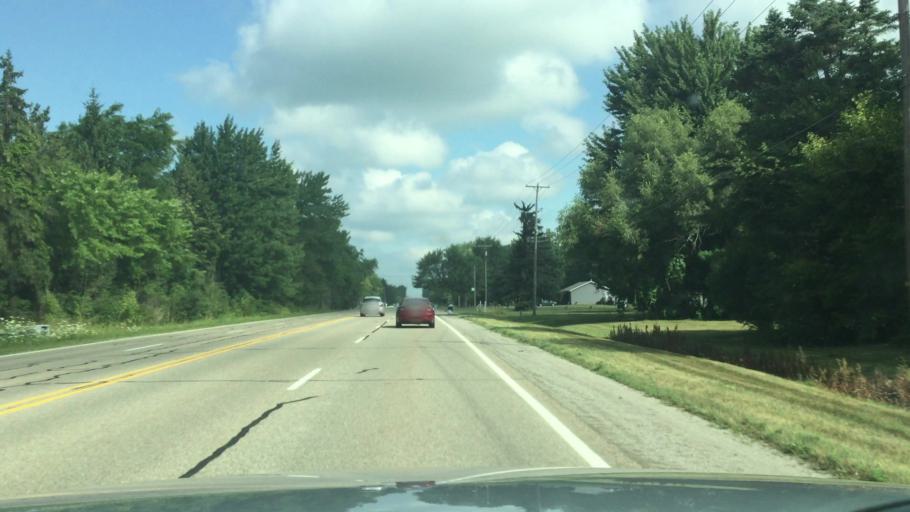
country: US
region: Michigan
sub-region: Genesee County
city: Clio
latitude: 43.2191
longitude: -83.7458
